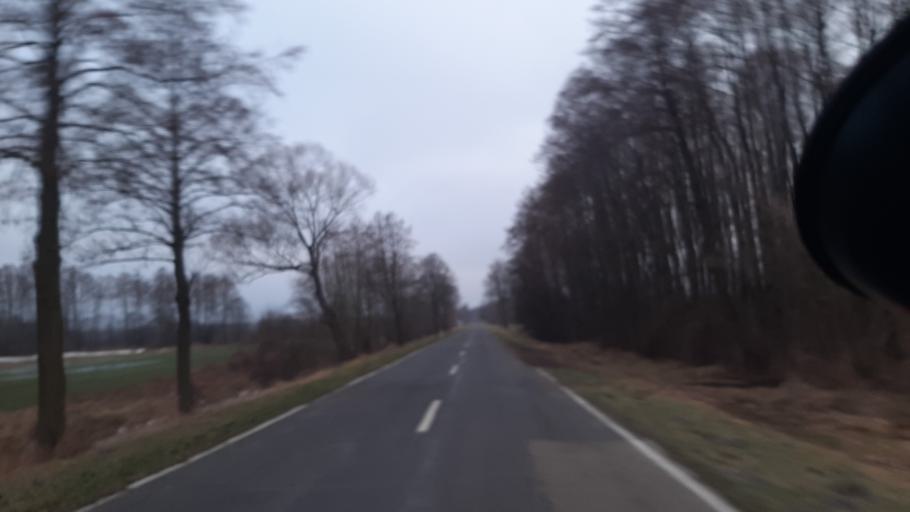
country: PL
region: Lublin Voivodeship
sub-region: Powiat parczewski
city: Podedworze
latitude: 51.5941
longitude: 23.1730
